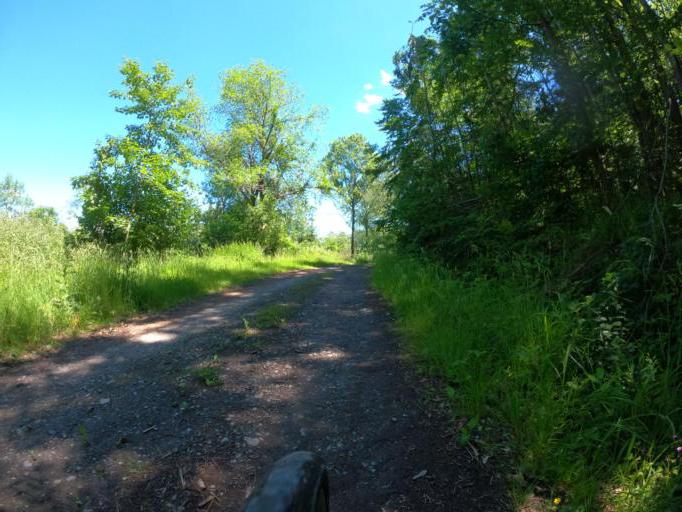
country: DE
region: Baden-Wuerttemberg
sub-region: Regierungsbezirk Stuttgart
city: Pfaffenhofen
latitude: 49.0104
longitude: 8.9821
